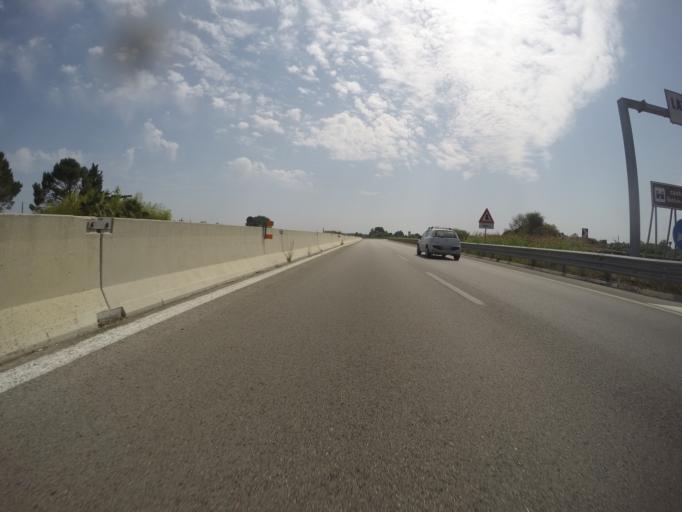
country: IT
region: Apulia
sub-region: Provincia di Brindisi
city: Latiano
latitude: 40.5600
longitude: 17.7266
